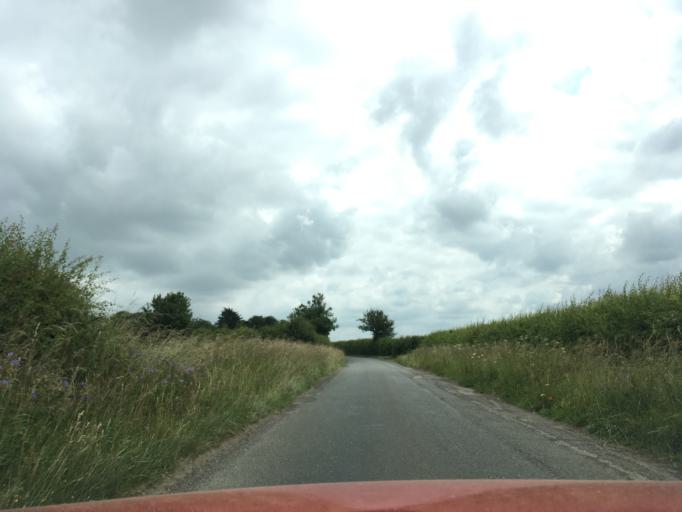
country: GB
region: England
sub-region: Oxfordshire
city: Chipping Norton
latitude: 51.9212
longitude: -1.5282
